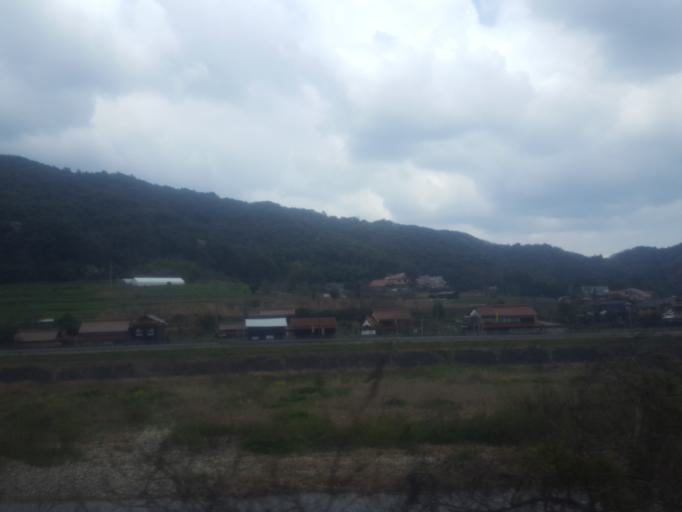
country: JP
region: Shimane
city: Masuda
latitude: 34.5746
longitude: 131.7972
